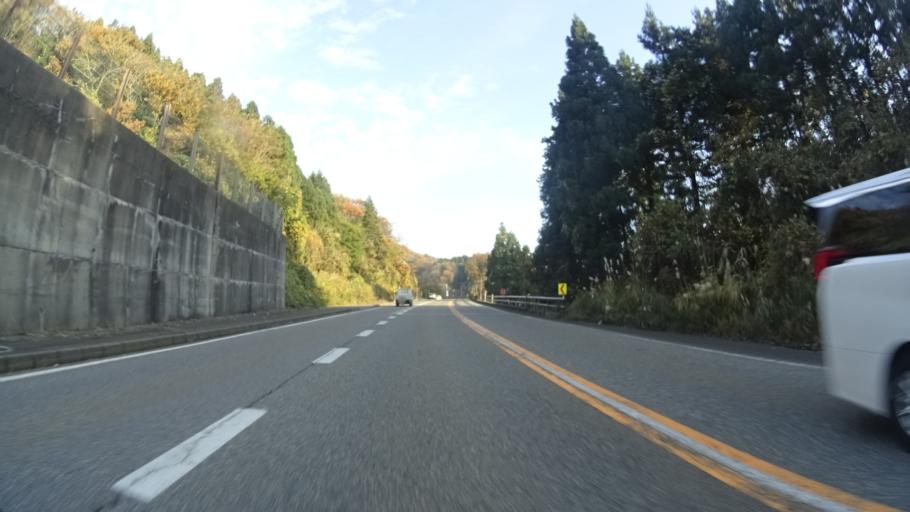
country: JP
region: Niigata
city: Kashiwazaki
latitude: 37.4063
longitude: 138.6536
